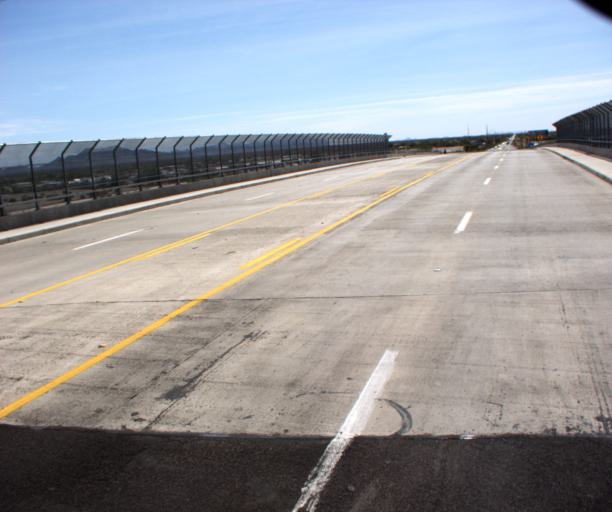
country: US
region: Arizona
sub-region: La Paz County
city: Quartzsite
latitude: 33.6636
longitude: -114.2172
